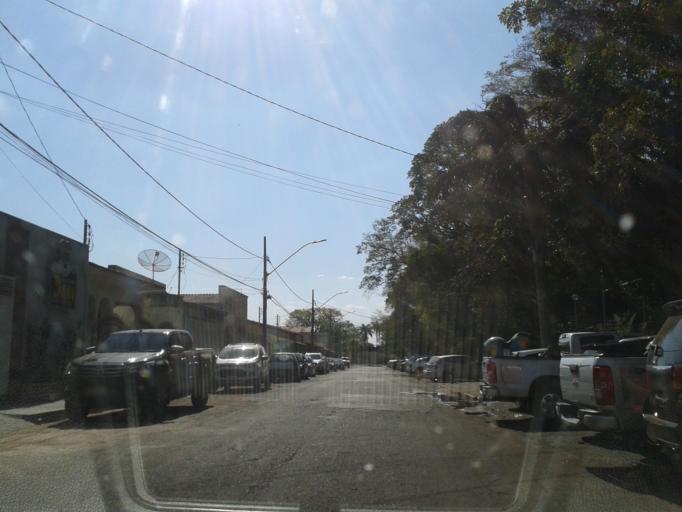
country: BR
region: Minas Gerais
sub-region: Araguari
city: Araguari
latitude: -18.6518
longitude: -48.1839
